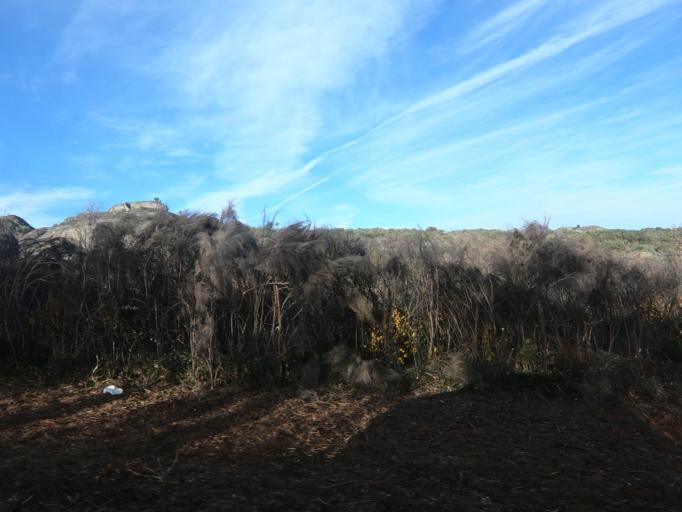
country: PT
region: Vila Real
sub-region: Sabrosa
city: Sabrosa
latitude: 41.3004
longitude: -7.6042
